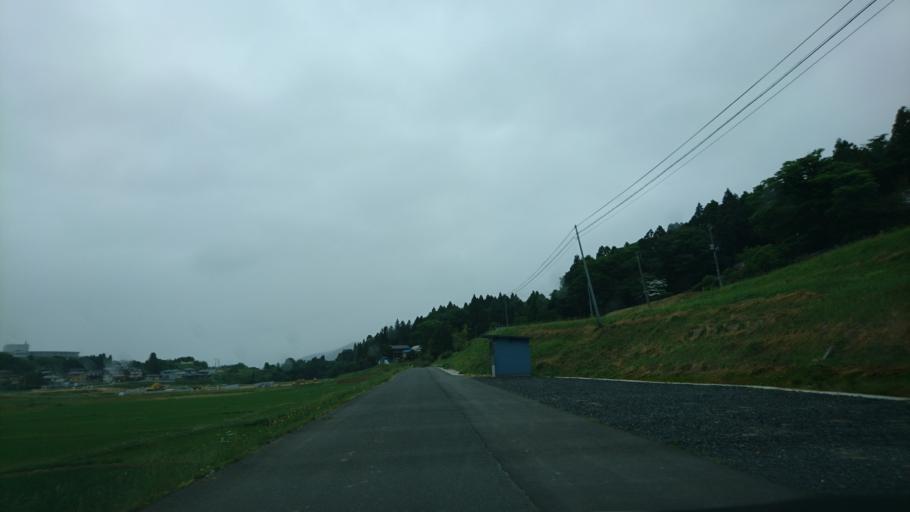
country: JP
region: Iwate
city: Ichinoseki
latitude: 38.9297
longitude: 141.1753
